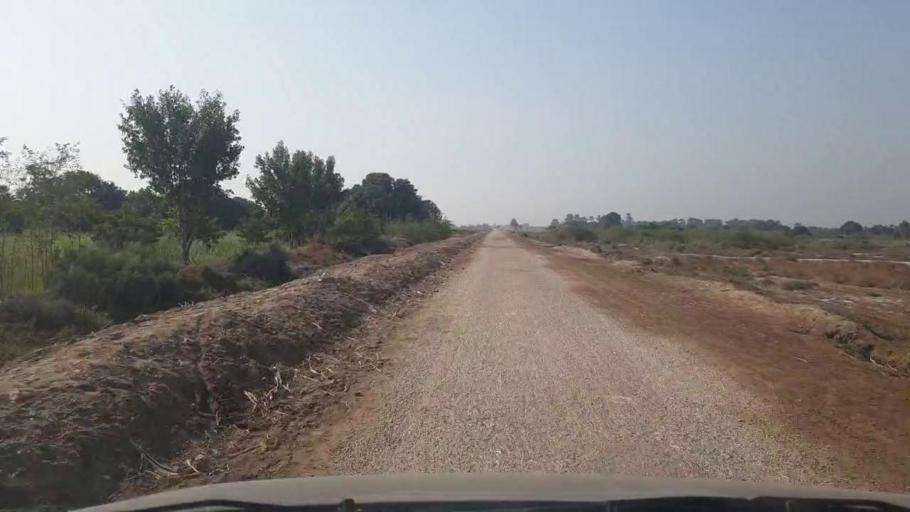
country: PK
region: Sindh
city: Mirwah Gorchani
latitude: 25.2707
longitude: 69.1179
